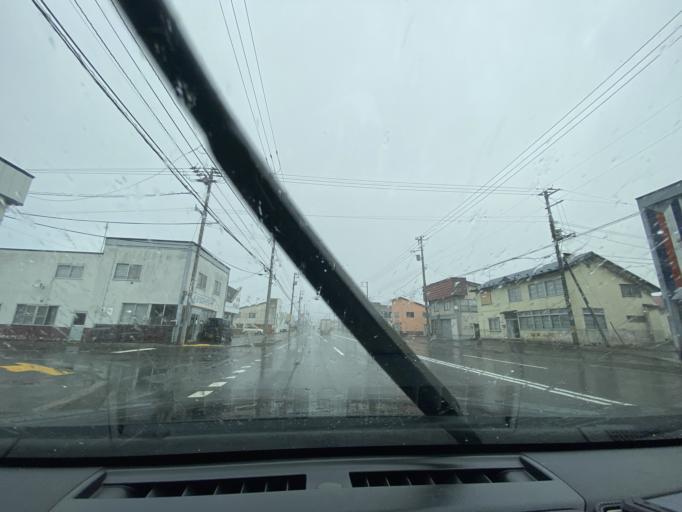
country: JP
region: Hokkaido
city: Takikawa
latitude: 43.6259
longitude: 141.9413
